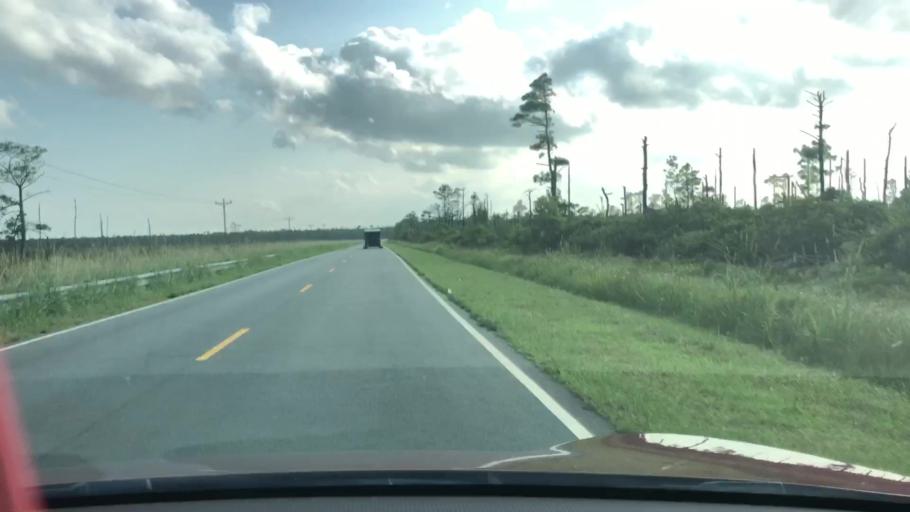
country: US
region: North Carolina
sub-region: Dare County
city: Wanchese
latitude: 35.6141
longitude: -75.7946
